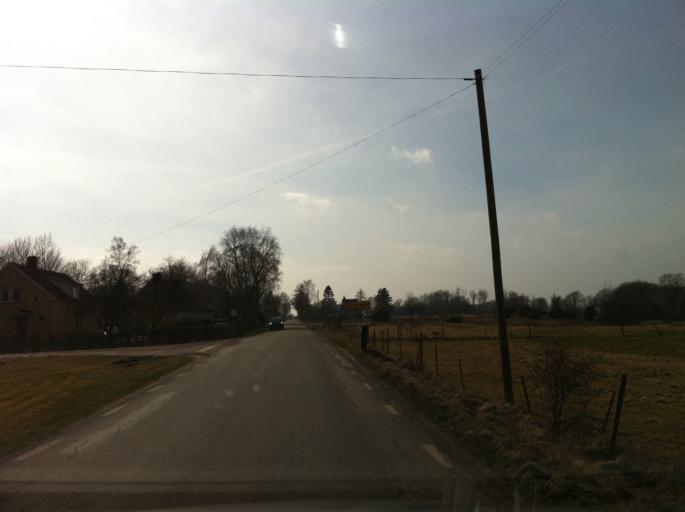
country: SE
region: Vaestra Goetaland
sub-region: Falkopings Kommun
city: Falkoeping
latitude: 58.2307
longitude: 13.4849
